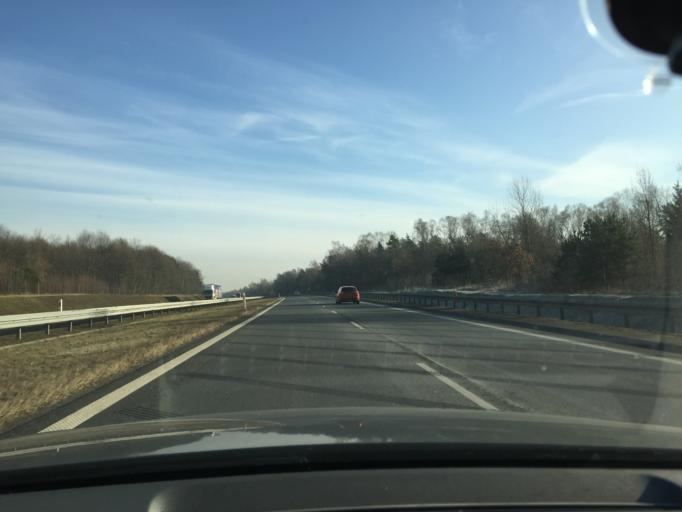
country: PL
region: Silesian Voivodeship
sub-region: Katowice
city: Murcki
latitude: 50.2213
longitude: 19.0972
